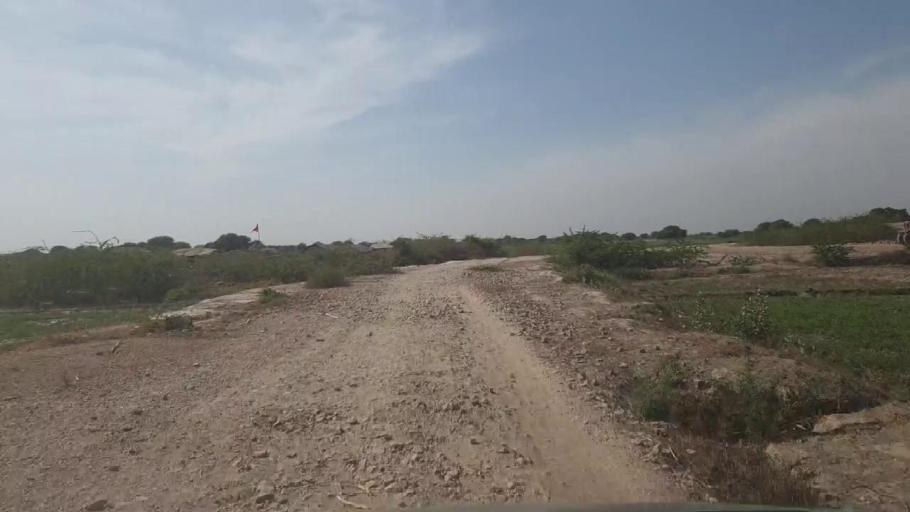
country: PK
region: Sindh
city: Nabisar
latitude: 25.1627
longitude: 69.6690
